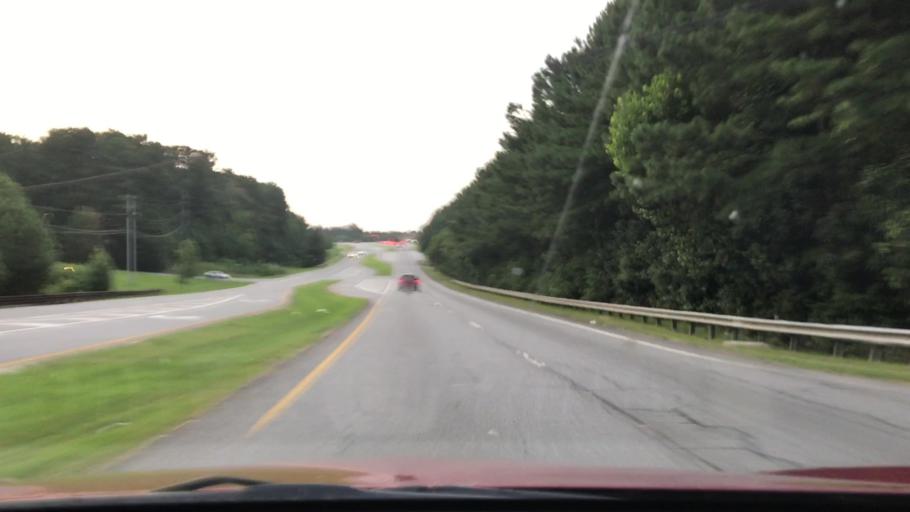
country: US
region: Georgia
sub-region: Gwinnett County
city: Lawrenceville
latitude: 34.0005
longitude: -83.9895
